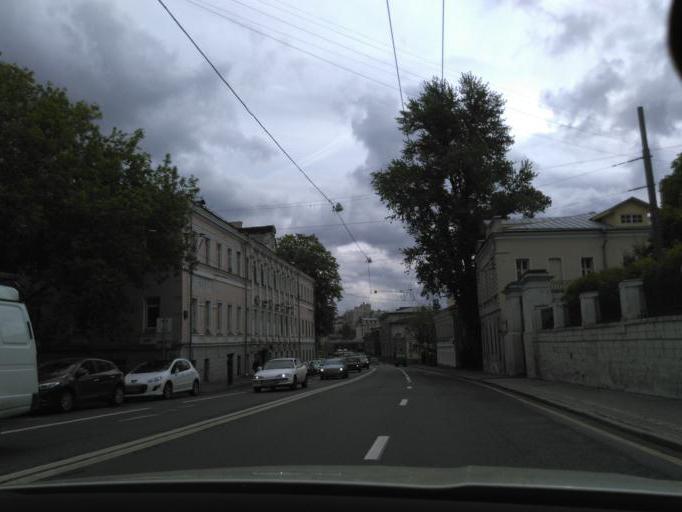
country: RU
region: Moscow
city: Zamoskvorech'ye
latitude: 55.7478
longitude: 37.6498
